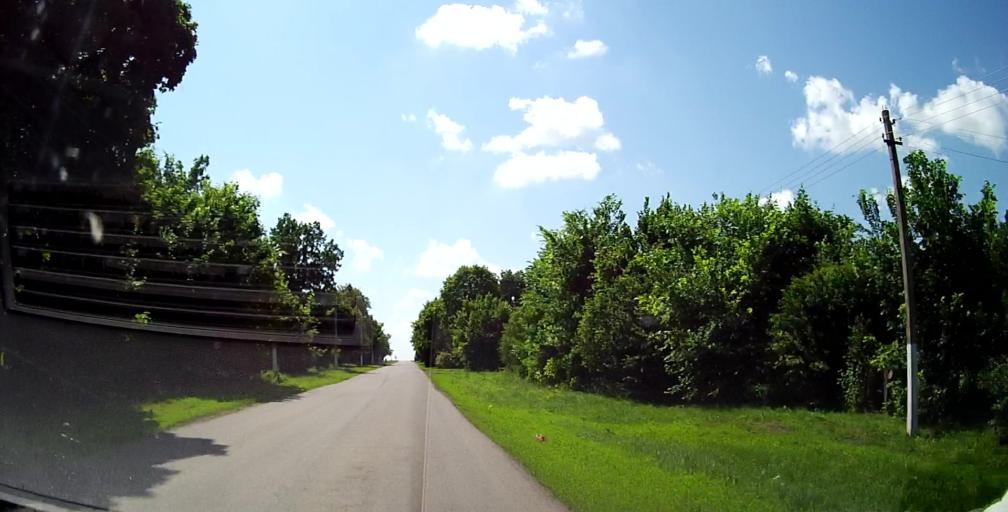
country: RU
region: Lipetsk
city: Chaplygin
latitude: 53.3212
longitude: 39.9562
